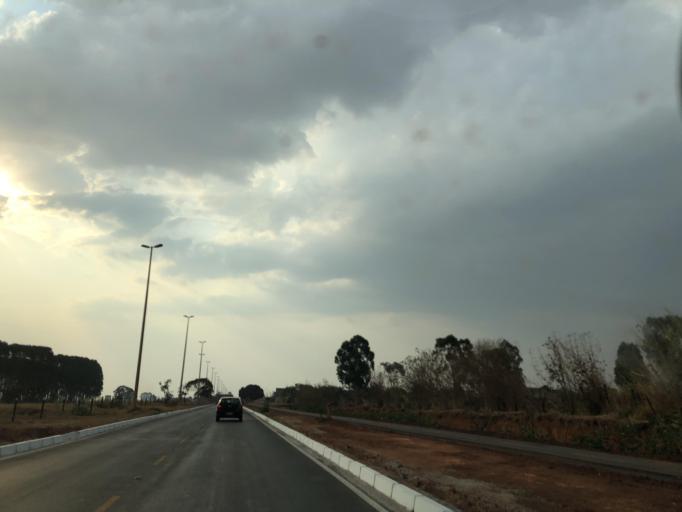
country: BR
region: Federal District
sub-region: Brasilia
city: Brasilia
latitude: -15.9287
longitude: -48.0497
